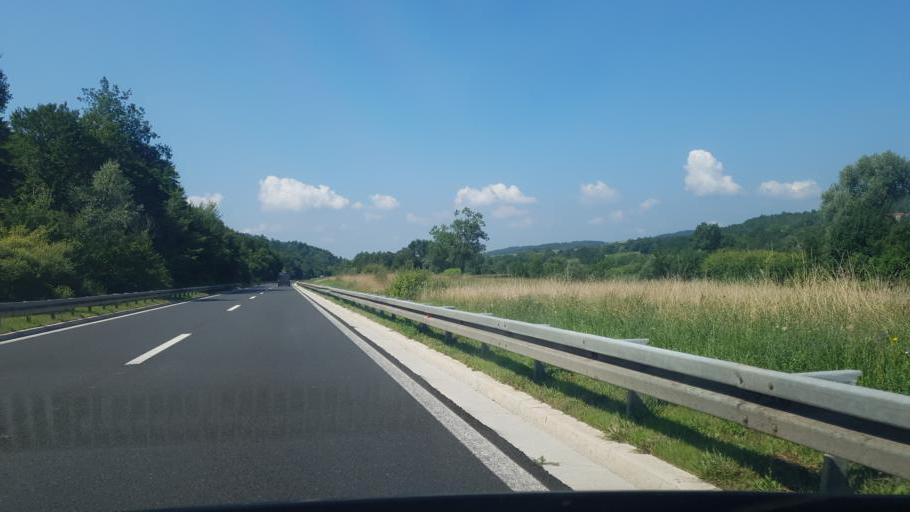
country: HR
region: Istarska
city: Pazin
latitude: 45.2976
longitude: 14.0465
